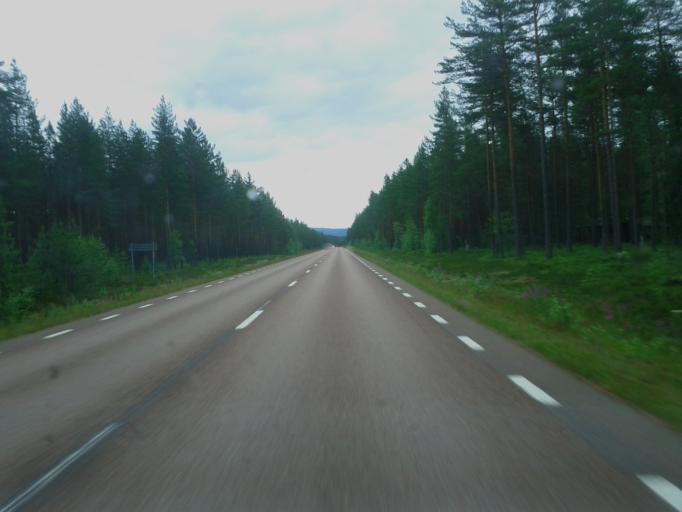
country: SE
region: Dalarna
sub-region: Alvdalens Kommun
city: AElvdalen
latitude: 61.2754
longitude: 13.9713
